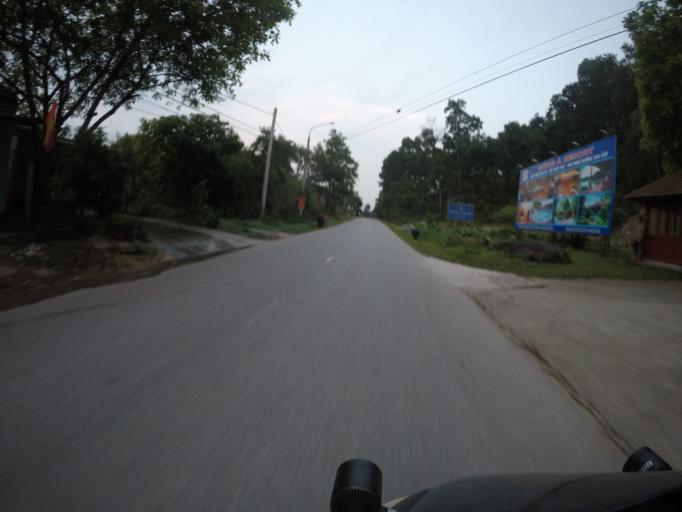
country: VN
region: Thai Nguyen
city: Chua Hang
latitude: 21.5869
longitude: 105.7338
